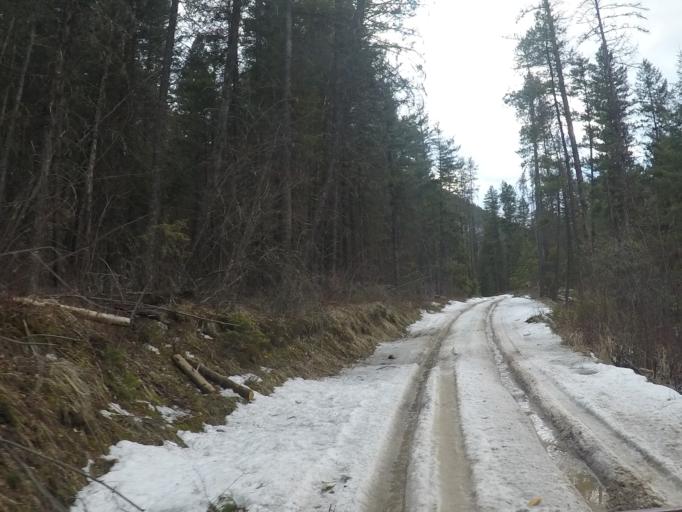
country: US
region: Montana
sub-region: Missoula County
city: Clinton
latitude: 46.5607
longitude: -113.7020
